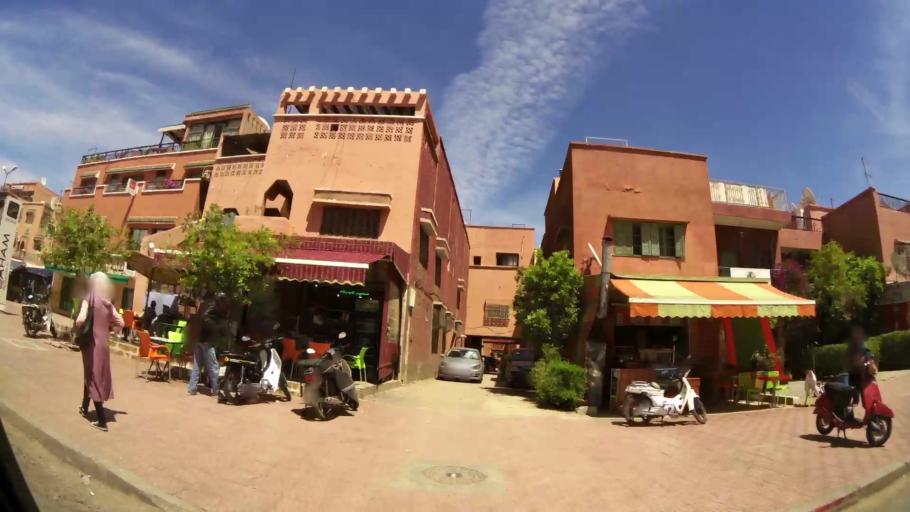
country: MA
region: Marrakech-Tensift-Al Haouz
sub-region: Marrakech
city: Marrakesh
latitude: 31.6553
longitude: -8.0032
